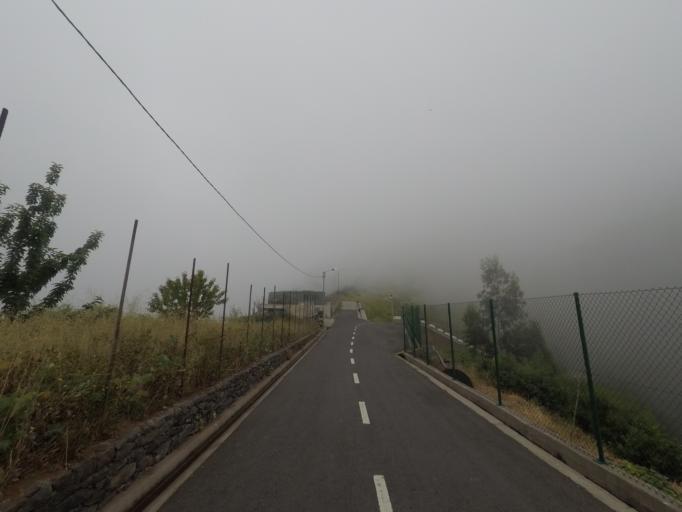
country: PT
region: Madeira
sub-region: Camara de Lobos
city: Curral das Freiras
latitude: 32.6900
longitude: -16.9475
